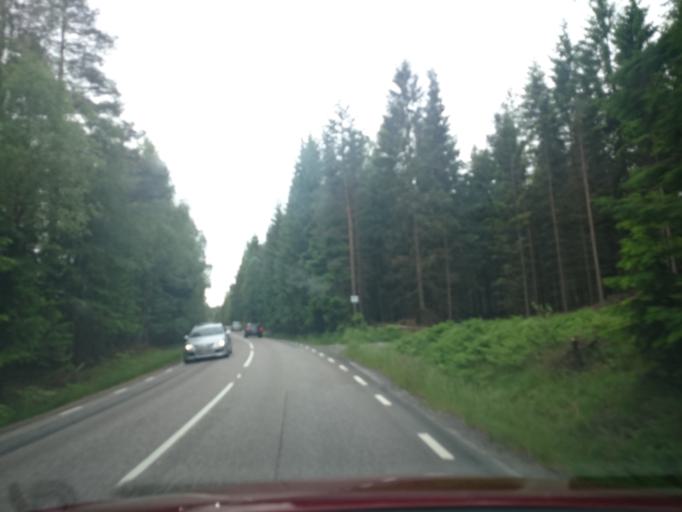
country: SE
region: Vaestra Goetaland
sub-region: Lerums Kommun
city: Stenkullen
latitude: 57.7195
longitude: 12.3460
